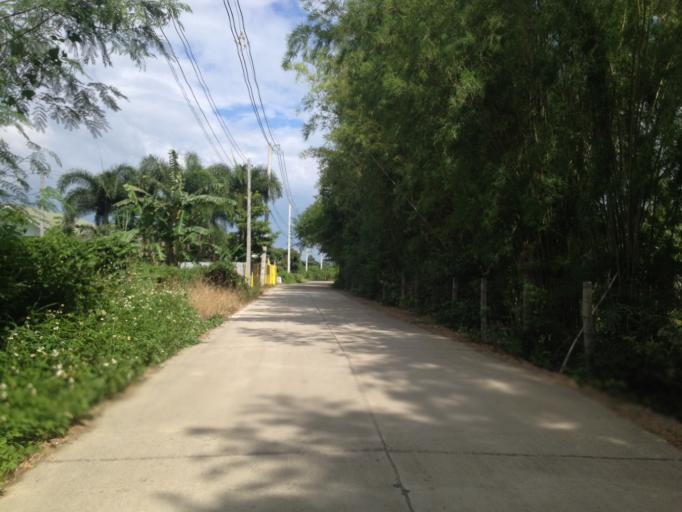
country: TH
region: Chiang Mai
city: Hang Dong
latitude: 18.6767
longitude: 98.8880
